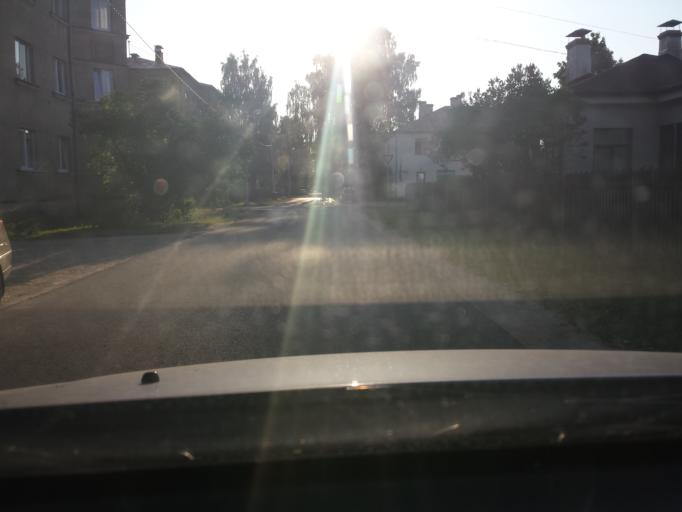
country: LV
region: Riga
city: Jaunciems
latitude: 56.9708
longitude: 24.1891
